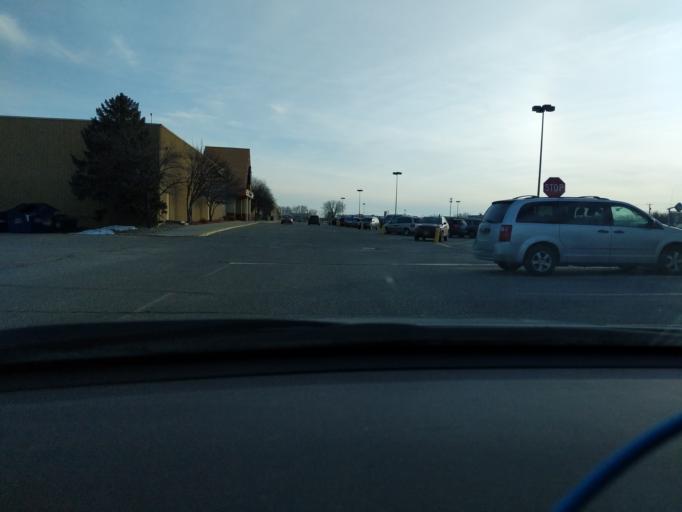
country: US
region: Minnesota
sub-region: Kandiyohi County
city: Willmar
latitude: 45.1071
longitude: -95.0408
